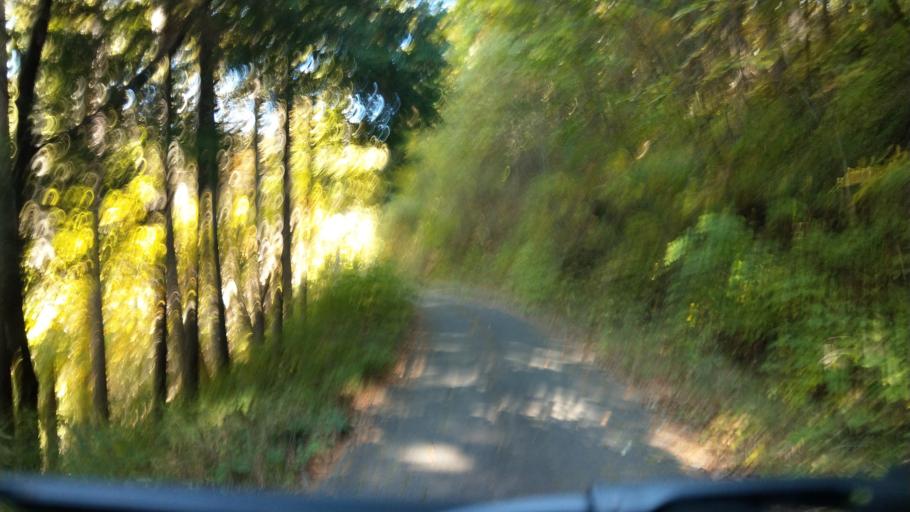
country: JP
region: Nagano
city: Komoro
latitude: 36.3727
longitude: 138.4454
